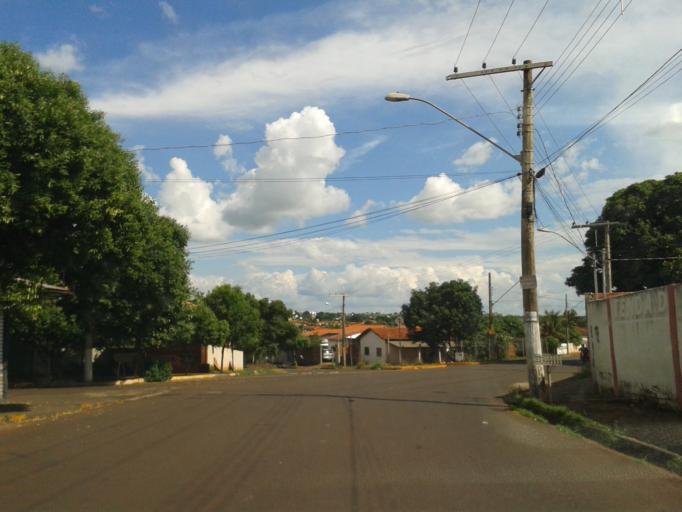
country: BR
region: Minas Gerais
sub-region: Ituiutaba
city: Ituiutaba
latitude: -18.9828
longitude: -49.4775
